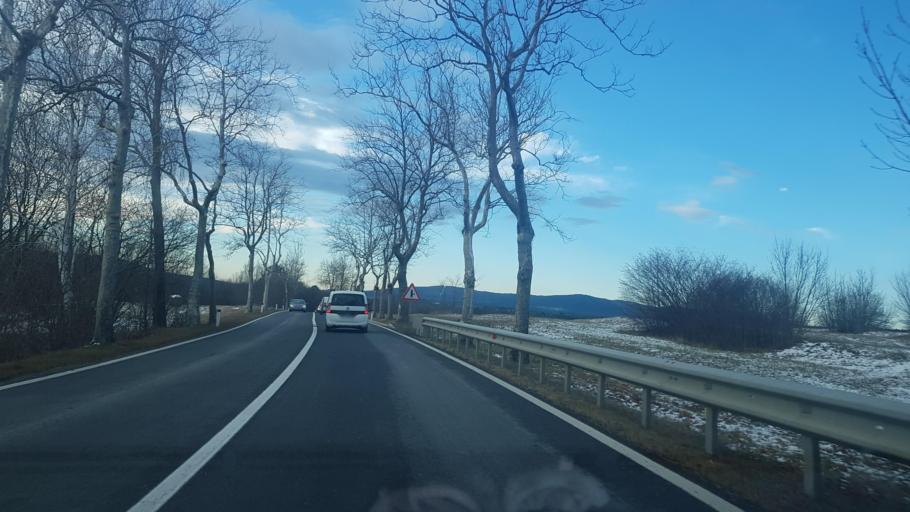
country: SI
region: Hrpelje-Kozina
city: Kozina
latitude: 45.5835
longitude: 13.9892
